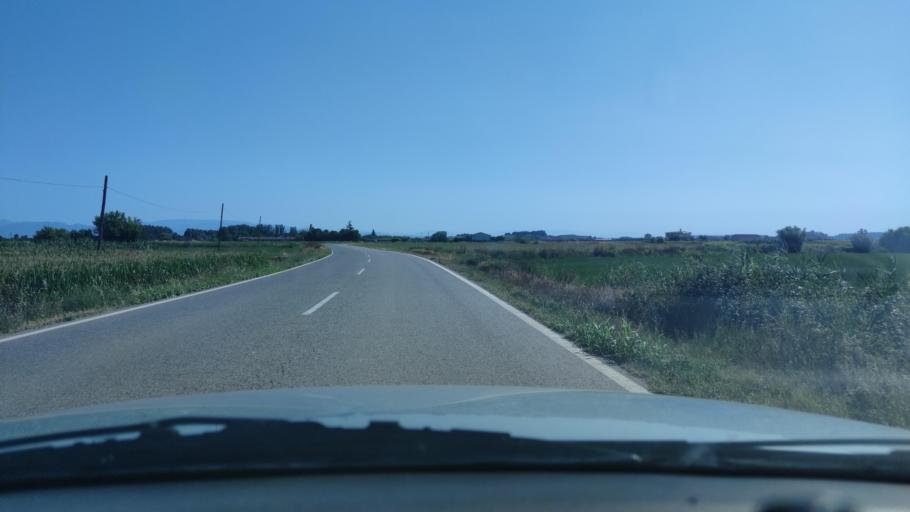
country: ES
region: Catalonia
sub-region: Provincia de Lleida
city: Bellvis
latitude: 41.6538
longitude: 0.8042
